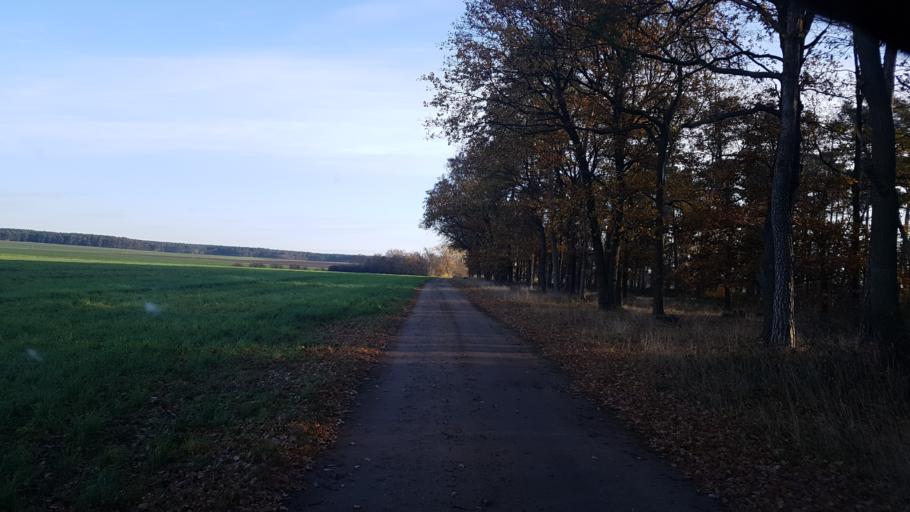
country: DE
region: Brandenburg
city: Sonnewalde
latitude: 51.6978
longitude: 13.6975
